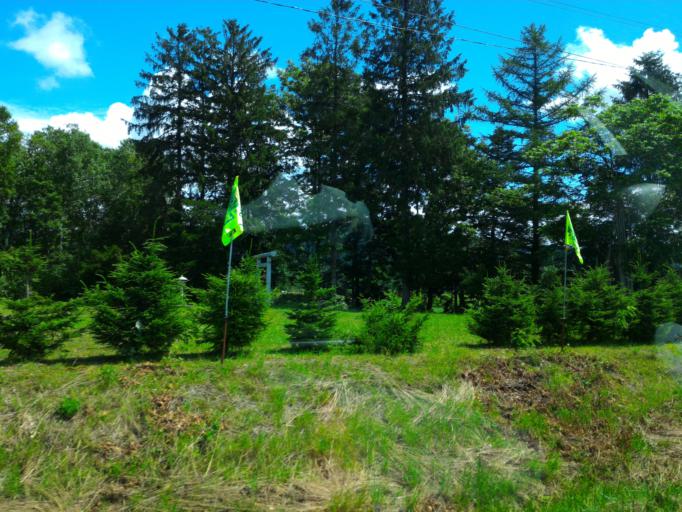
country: JP
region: Hokkaido
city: Nayoro
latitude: 44.5728
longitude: 142.3131
